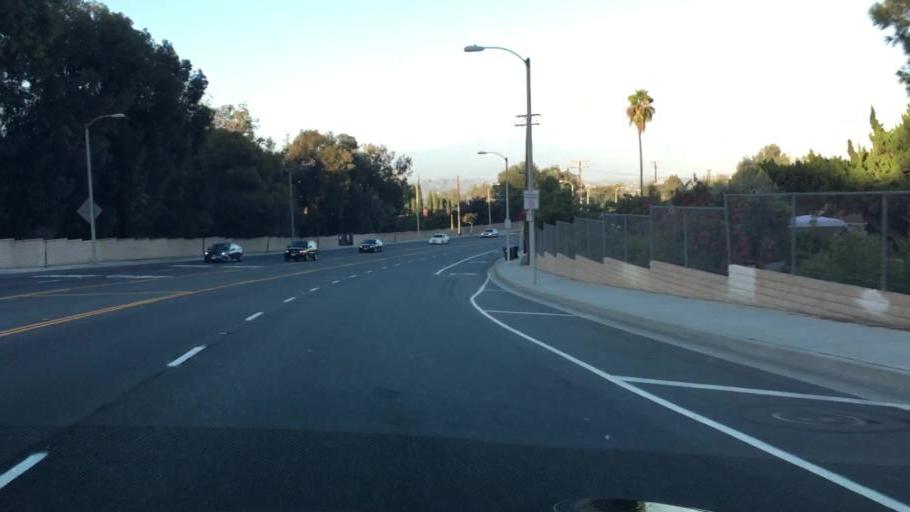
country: US
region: California
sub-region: Los Angeles County
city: Rowland Heights
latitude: 33.9686
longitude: -117.9149
